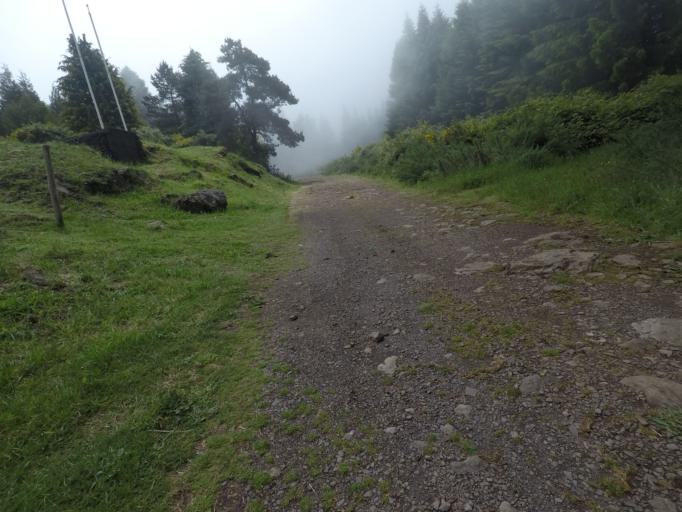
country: PT
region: Madeira
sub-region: Sao Vicente
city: Sao Vicente
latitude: 32.7704
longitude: -17.0761
